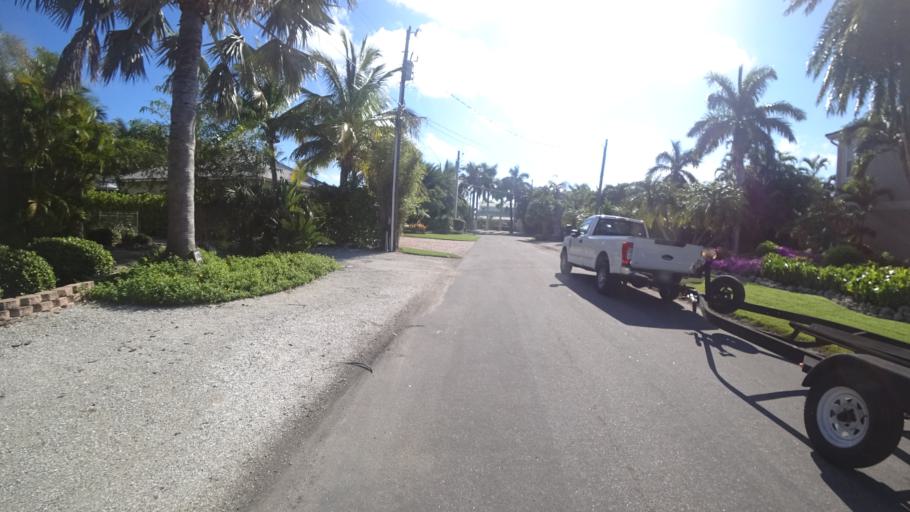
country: US
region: Florida
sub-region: Manatee County
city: Anna Maria
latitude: 27.5291
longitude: -82.7268
